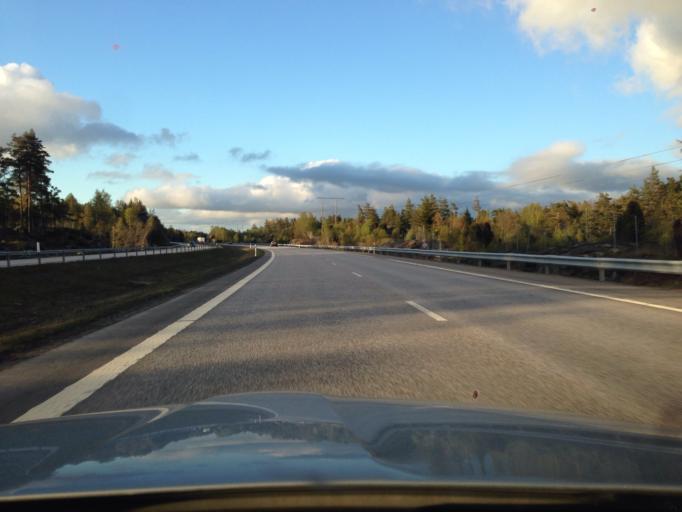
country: SE
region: Soedermanland
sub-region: Oxelosunds Kommun
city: Oxelosund
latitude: 58.8288
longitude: 17.1624
